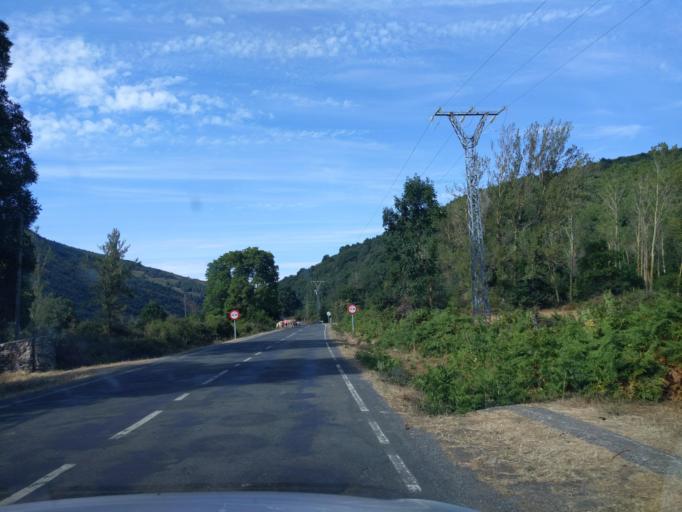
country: ES
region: La Rioja
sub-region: Provincia de La Rioja
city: Ezcaray
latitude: 42.2927
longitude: -3.0251
